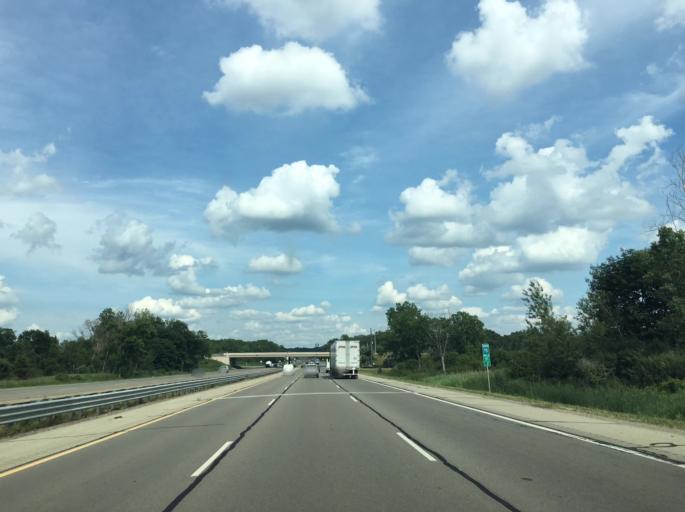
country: US
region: Michigan
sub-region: Oakland County
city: Clarkston
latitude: 42.7466
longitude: -83.4235
